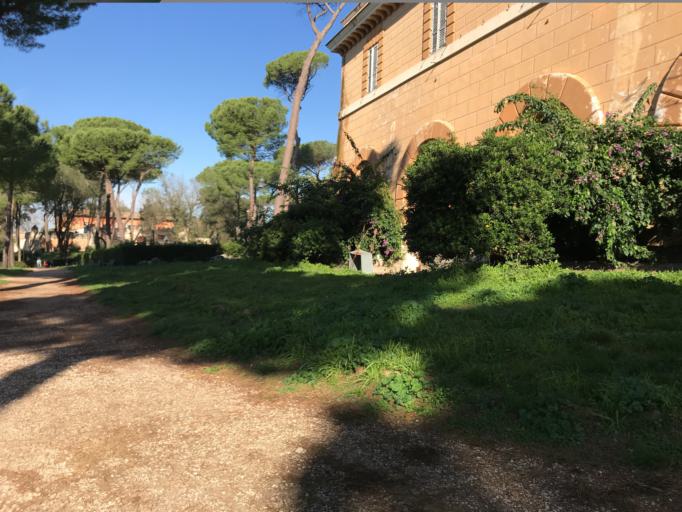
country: IT
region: Latium
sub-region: Citta metropolitana di Roma Capitale
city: Rome
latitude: 41.9140
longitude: 12.4875
